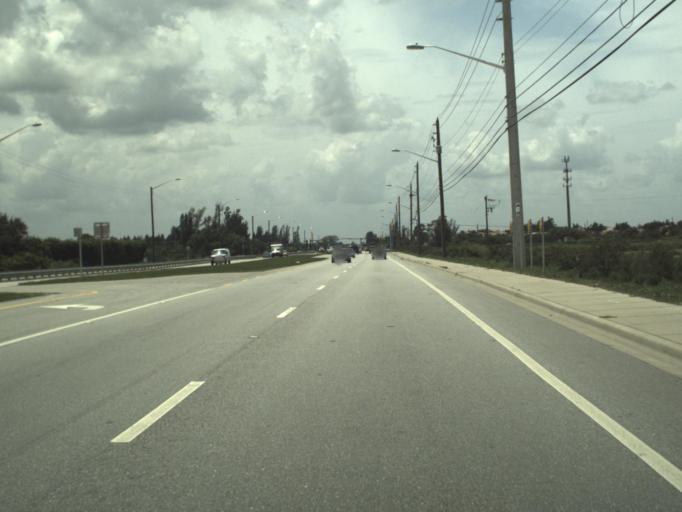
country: US
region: Florida
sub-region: Palm Beach County
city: Villages of Oriole
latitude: 26.4539
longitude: -80.1816
